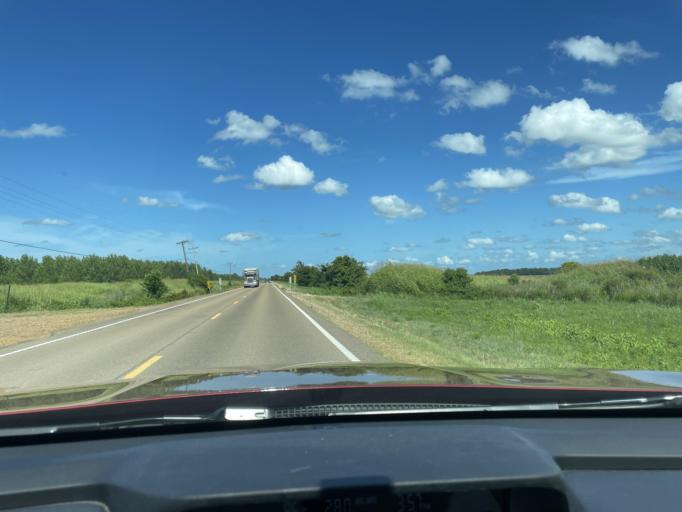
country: US
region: Mississippi
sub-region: Humphreys County
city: Belzoni
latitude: 33.1829
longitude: -90.6162
